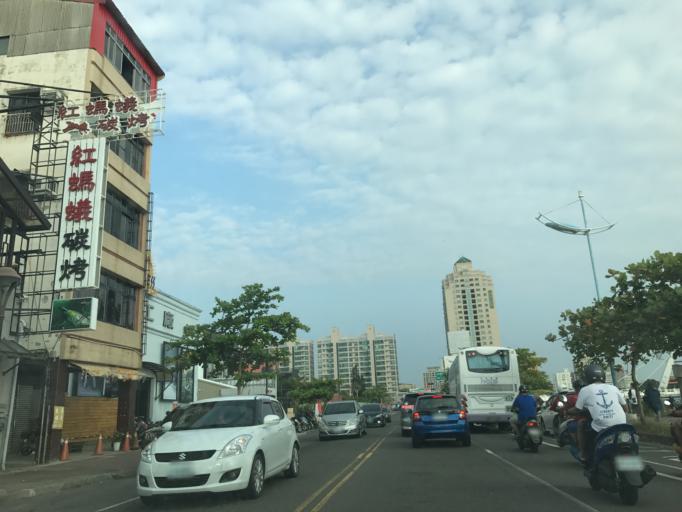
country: TW
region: Taiwan
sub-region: Tainan
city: Tainan
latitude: 22.9980
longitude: 120.1852
